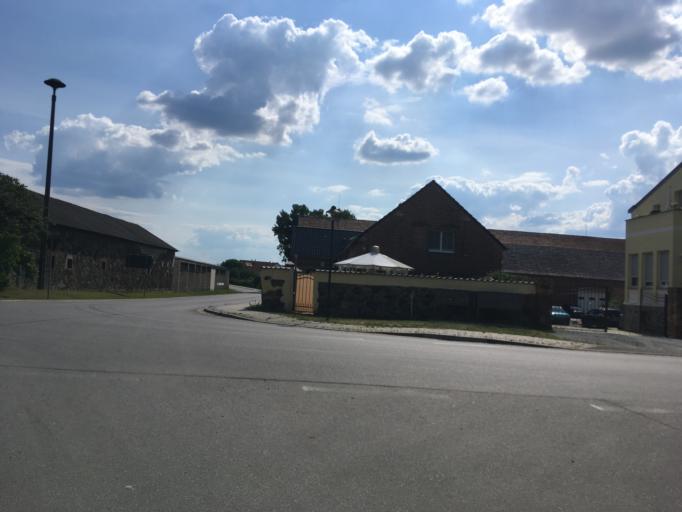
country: DE
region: Brandenburg
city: Steinhofel
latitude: 52.4241
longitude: 14.1114
